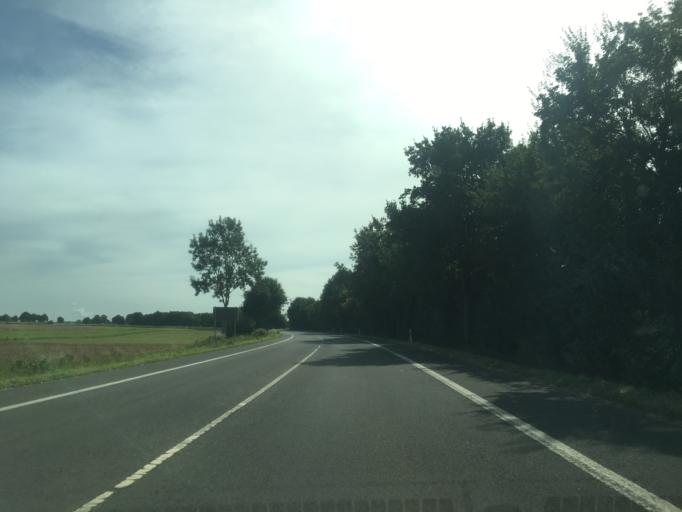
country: DE
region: North Rhine-Westphalia
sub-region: Regierungsbezirk Koln
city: Titz
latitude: 51.0418
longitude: 6.3982
